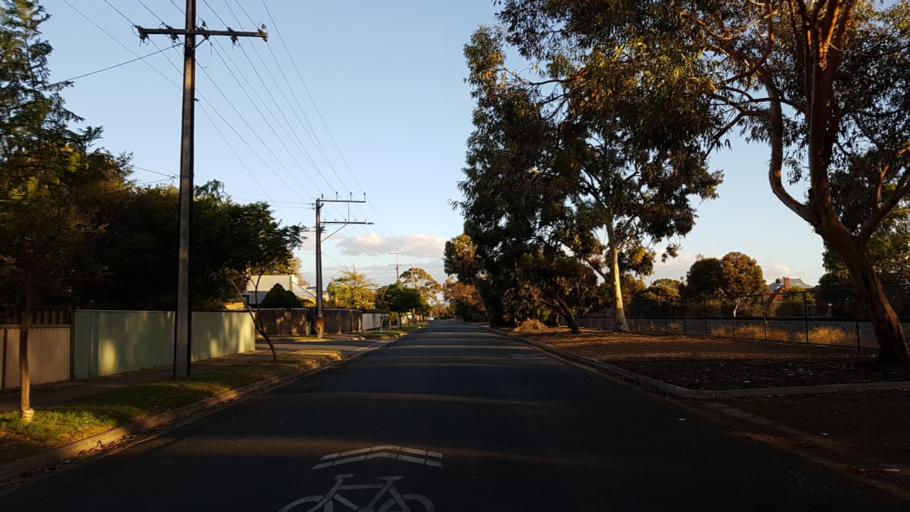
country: AU
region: South Australia
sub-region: Port Adelaide Enfield
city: Alberton
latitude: -34.8637
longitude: 138.5232
